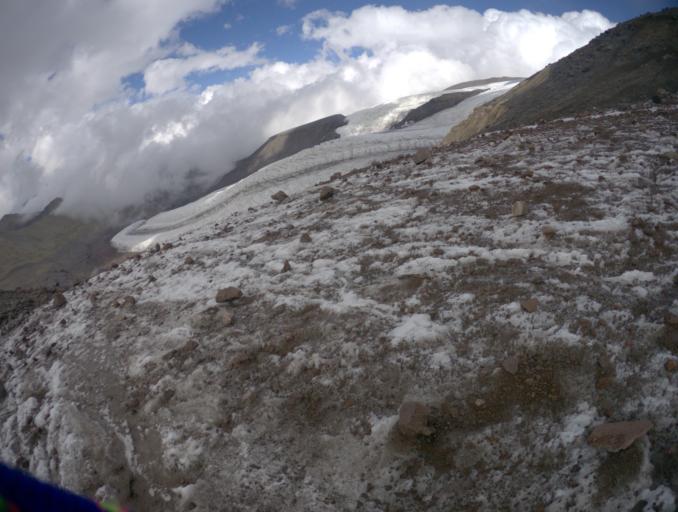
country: RU
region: Kabardino-Balkariya
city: Terskol
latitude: 43.3827
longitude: 42.4161
